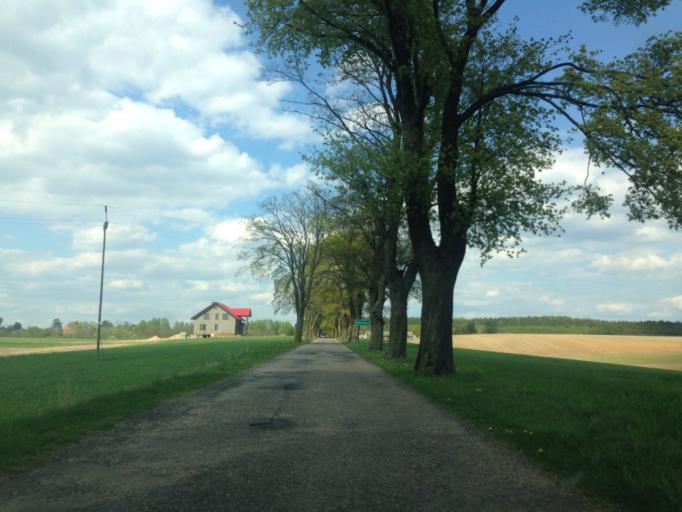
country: PL
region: Kujawsko-Pomorskie
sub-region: Powiat brodnicki
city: Bartniczka
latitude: 53.2807
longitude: 19.6904
